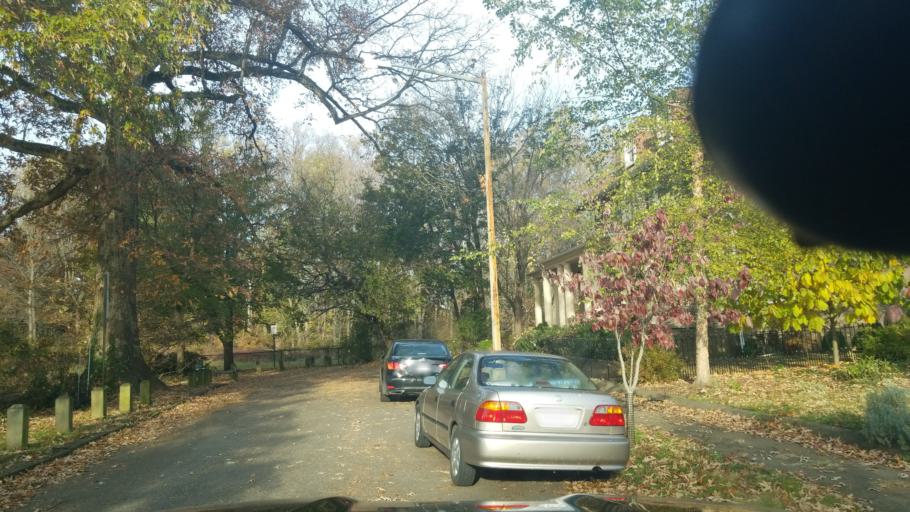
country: US
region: Maryland
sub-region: Montgomery County
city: Silver Spring
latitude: 38.9572
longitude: -77.0381
